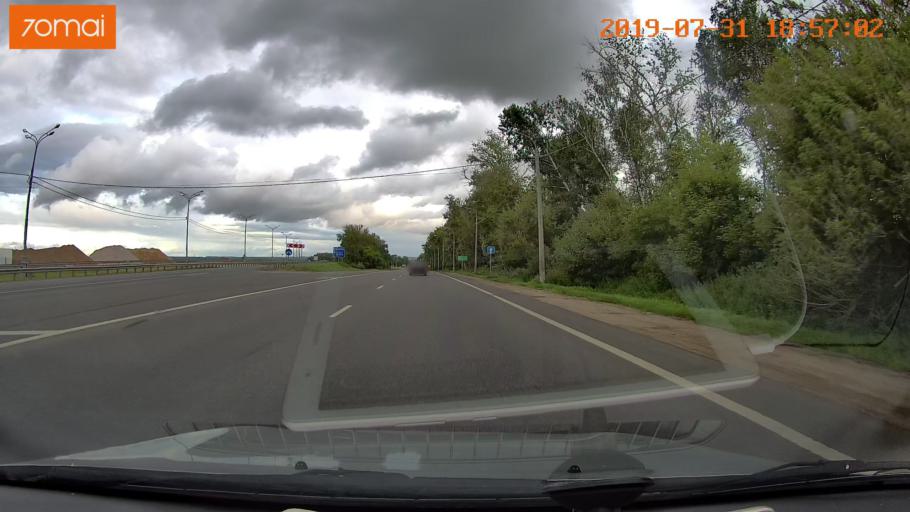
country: RU
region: Moskovskaya
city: Raduzhnyy
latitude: 55.1575
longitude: 38.6867
